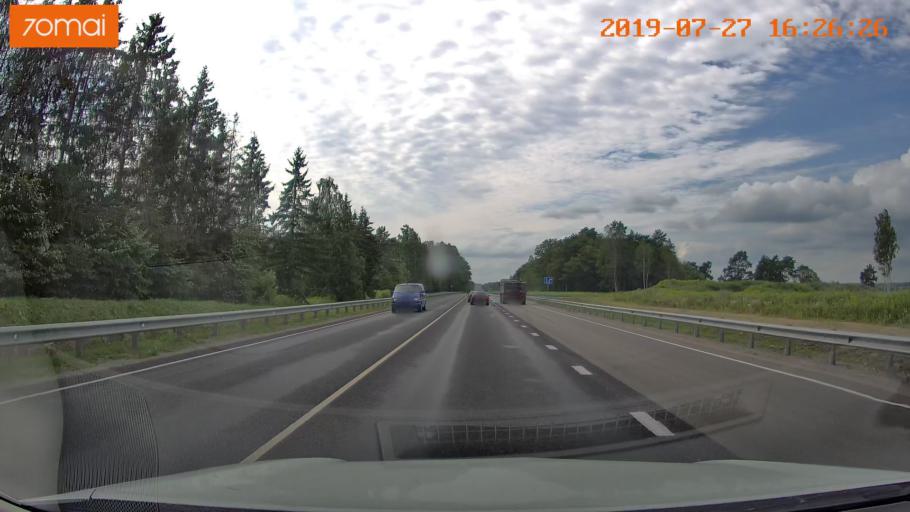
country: RU
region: Kaliningrad
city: Zheleznodorozhnyy
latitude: 54.6403
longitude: 21.4106
